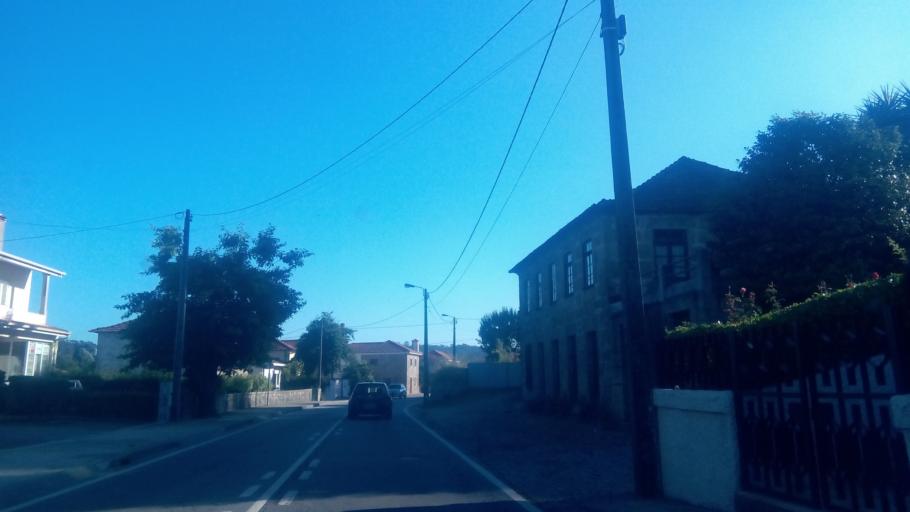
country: PT
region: Porto
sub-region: Paredes
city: Madalena
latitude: 41.2347
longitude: -8.3623
